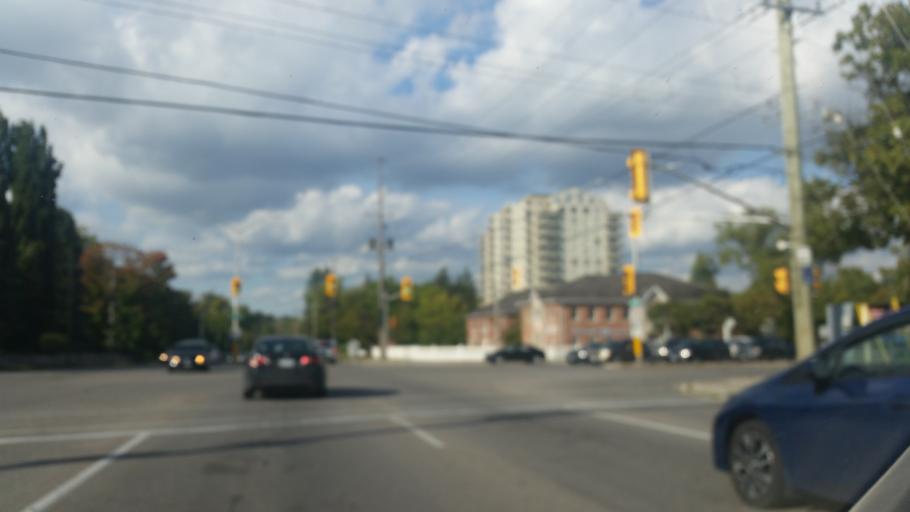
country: CA
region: Ontario
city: London
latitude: 42.9634
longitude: -81.2929
